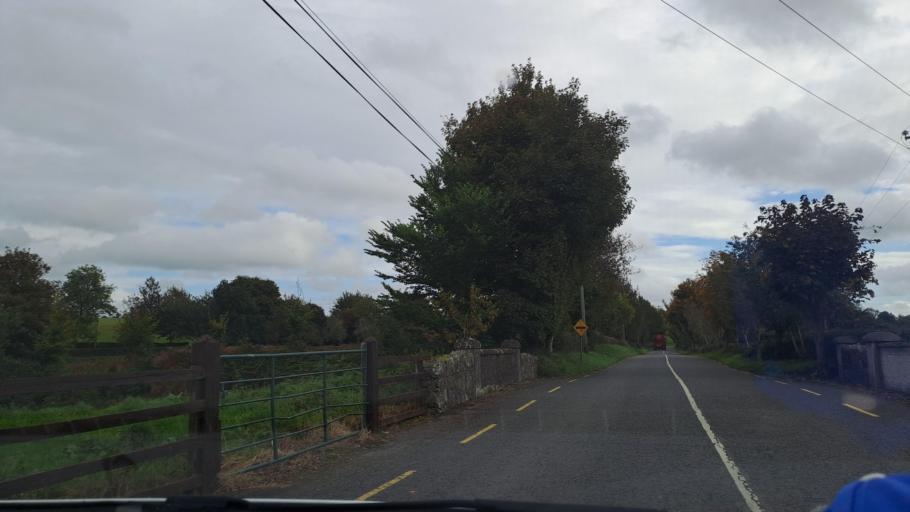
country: IE
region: Ulster
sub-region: An Cabhan
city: Kingscourt
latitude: 53.9390
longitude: -6.7837
